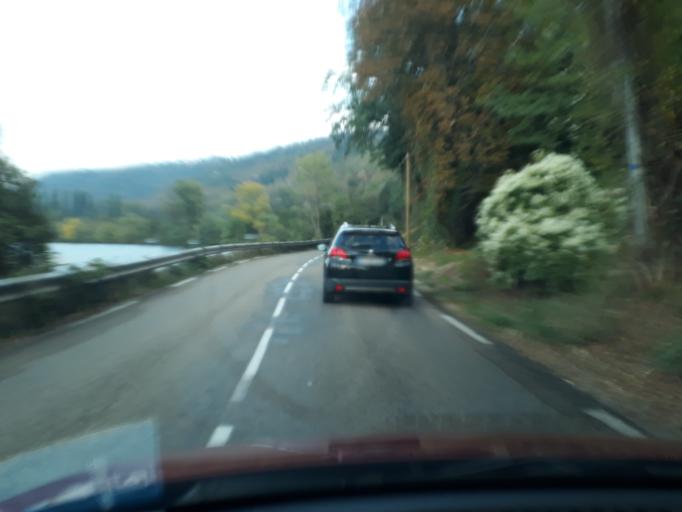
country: FR
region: Rhone-Alpes
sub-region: Departement de l'Isere
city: Les Roches-de-Condrieu
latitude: 45.4545
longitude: 4.7801
